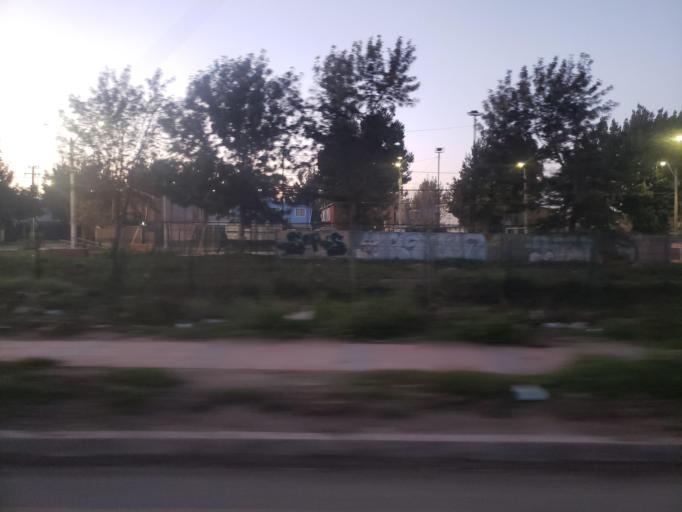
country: CL
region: Santiago Metropolitan
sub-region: Provincia de Talagante
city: El Monte
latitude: -33.6841
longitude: -71.0041
